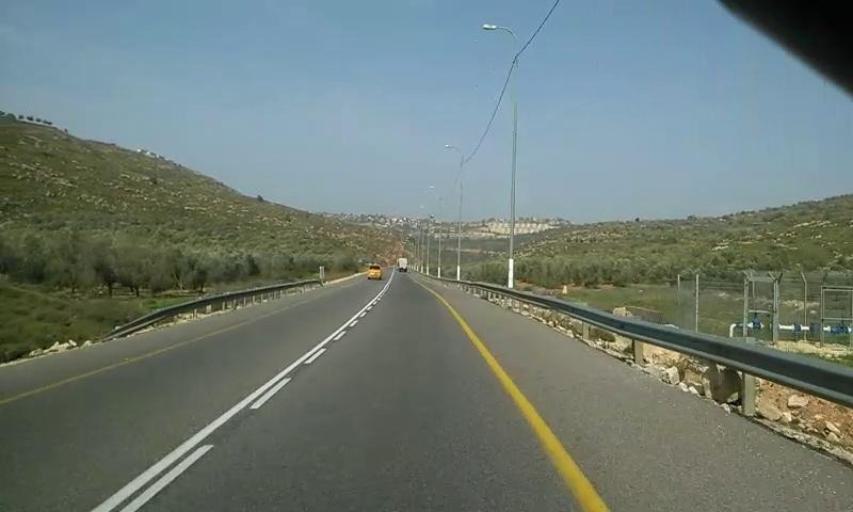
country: PS
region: West Bank
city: Qaryut
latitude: 32.0616
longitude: 35.2786
